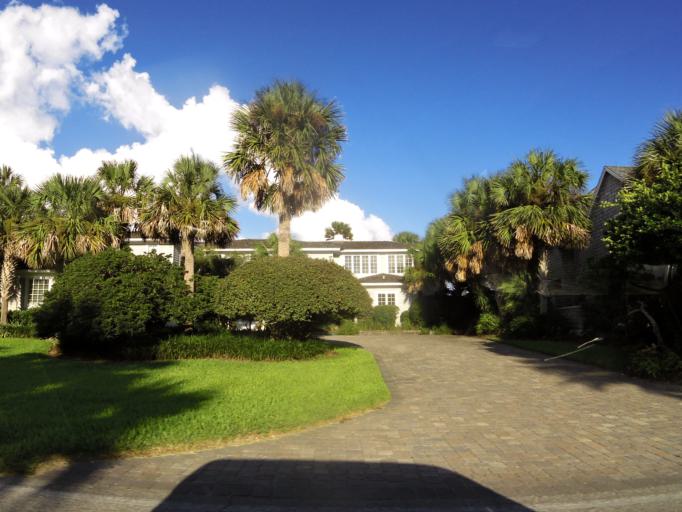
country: US
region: Florida
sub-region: Saint Johns County
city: Ponte Vedra Beach
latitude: 30.2358
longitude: -81.3769
